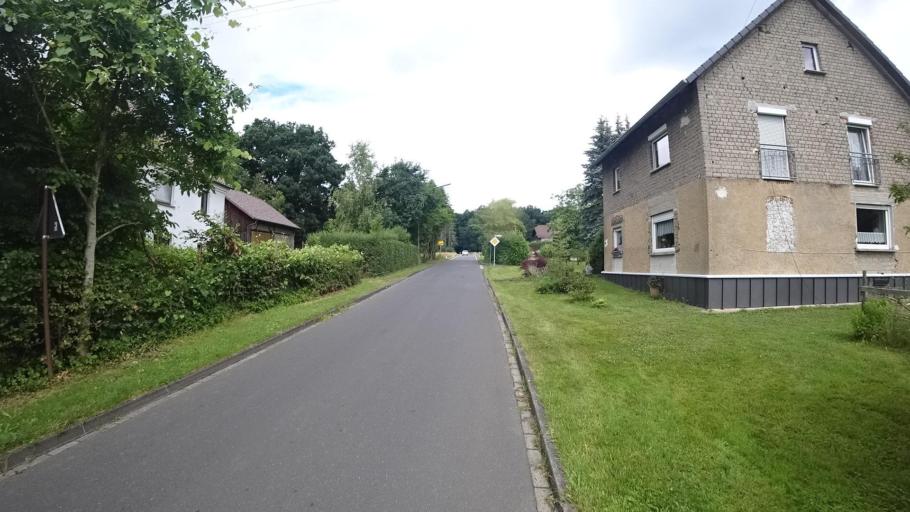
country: DE
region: Rheinland-Pfalz
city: Hirz-Maulsbach
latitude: 50.6851
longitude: 7.4701
